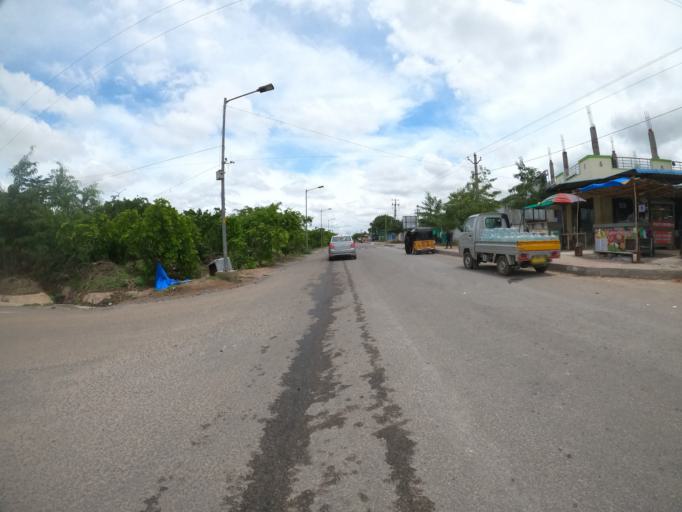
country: IN
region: Telangana
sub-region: Hyderabad
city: Hyderabad
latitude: 17.3395
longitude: 78.3666
